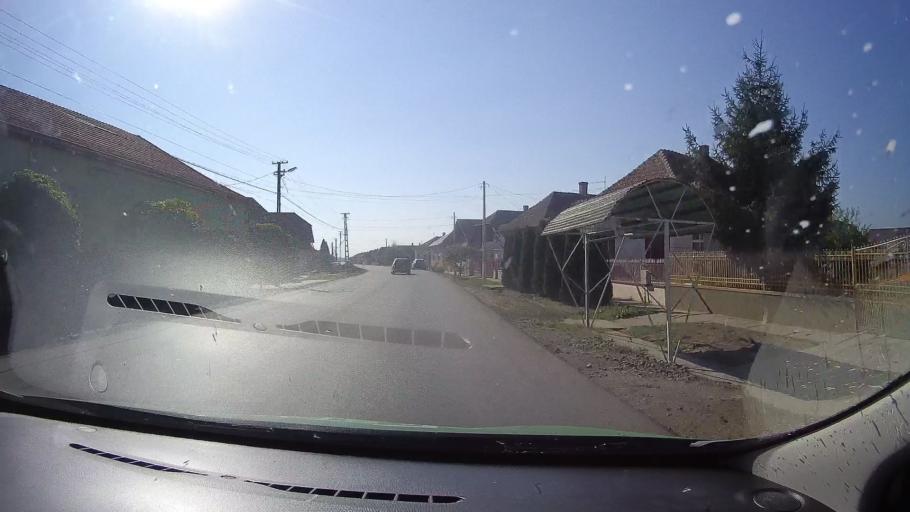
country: RO
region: Satu Mare
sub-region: Comuna Camin
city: Camin
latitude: 47.7277
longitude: 22.4767
